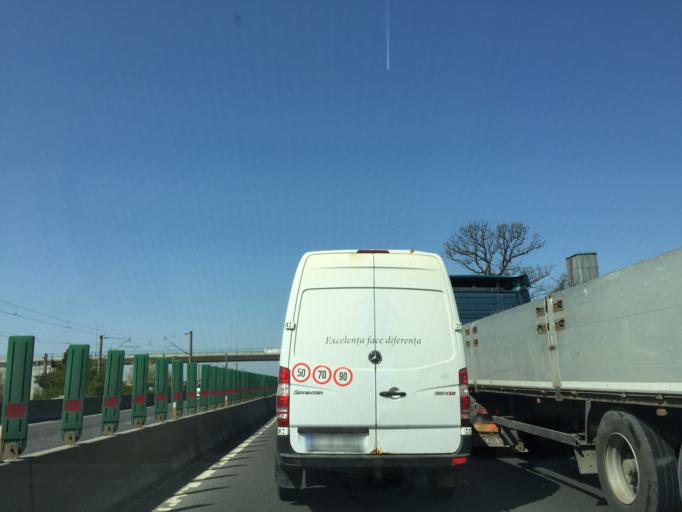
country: RO
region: Ilfov
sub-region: Comuna Tunari
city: Tunari
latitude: 44.5353
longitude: 26.1444
